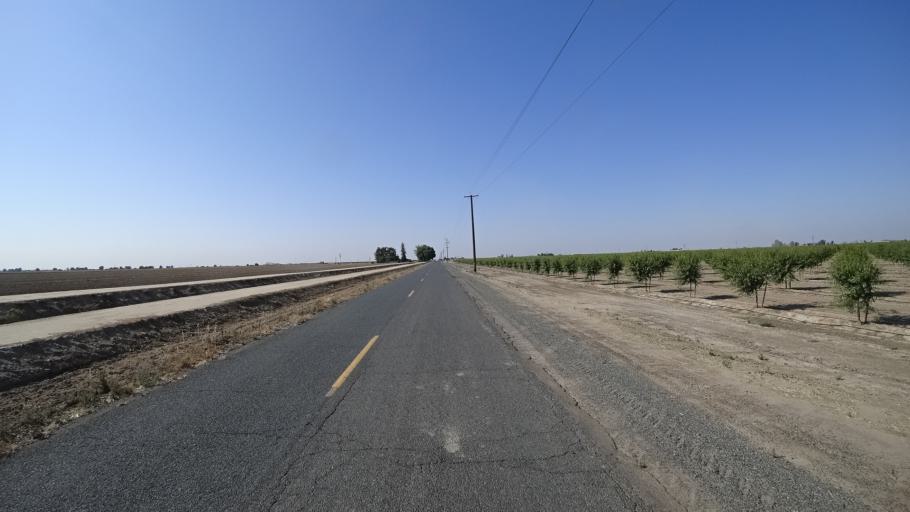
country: US
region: California
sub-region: Kings County
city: Home Garden
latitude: 36.2394
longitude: -119.5831
